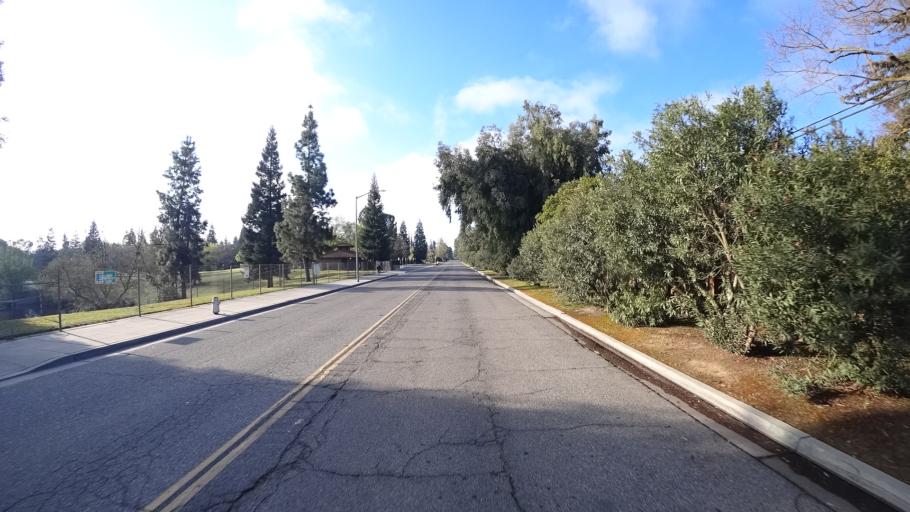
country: US
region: California
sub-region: Fresno County
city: Fresno
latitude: 36.8180
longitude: -119.8309
